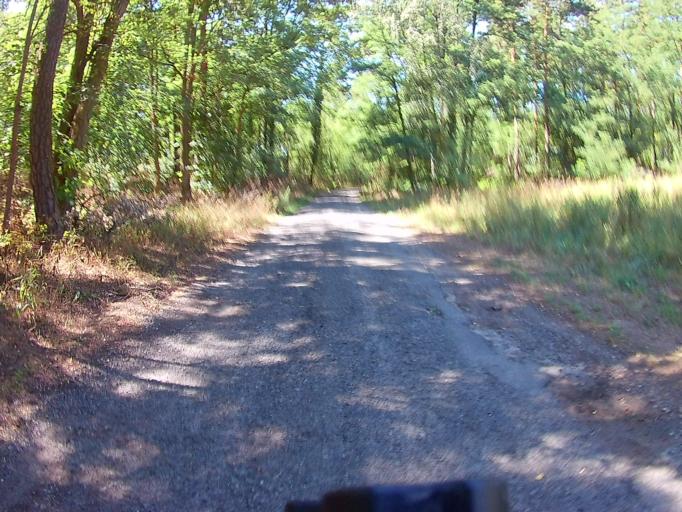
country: DE
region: Brandenburg
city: Baruth
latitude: 52.1139
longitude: 13.5281
